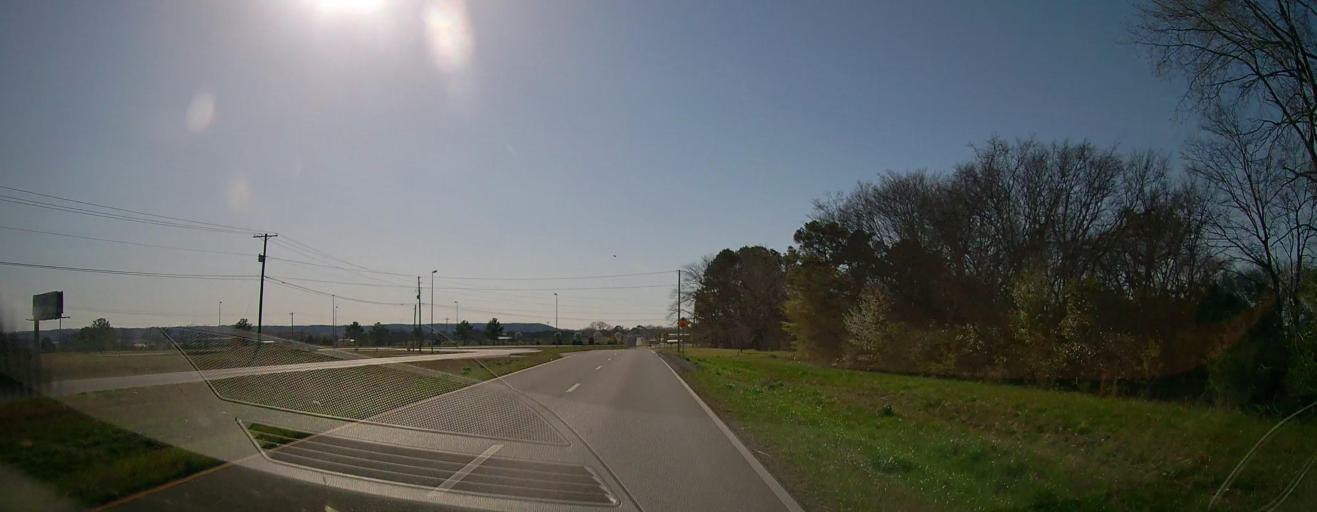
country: US
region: Alabama
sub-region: Colbert County
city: Muscle Shoals
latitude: 34.7006
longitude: -87.6381
